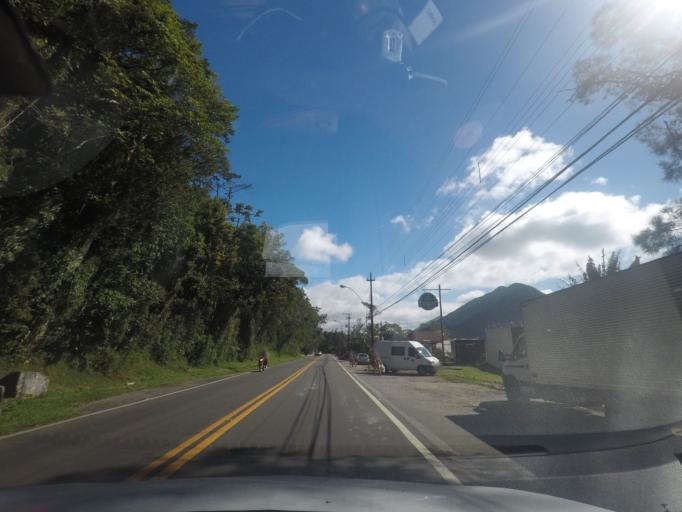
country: BR
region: Rio de Janeiro
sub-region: Teresopolis
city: Teresopolis
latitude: -22.4550
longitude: -42.9841
